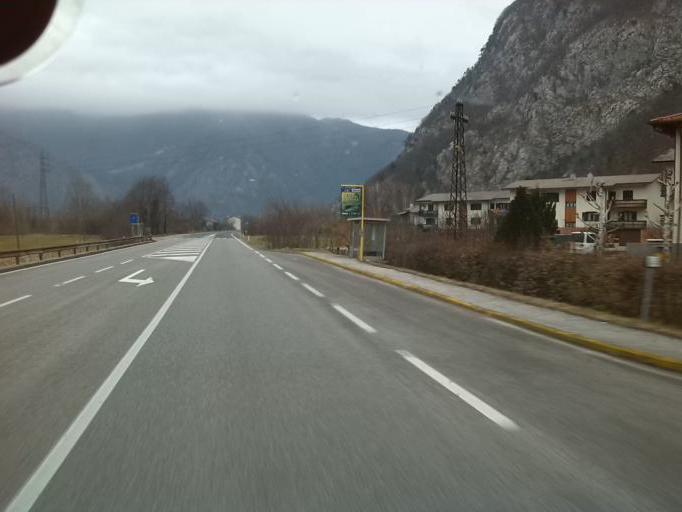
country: IT
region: Friuli Venezia Giulia
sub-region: Provincia di Udine
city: Venzone
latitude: 46.3577
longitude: 13.1378
